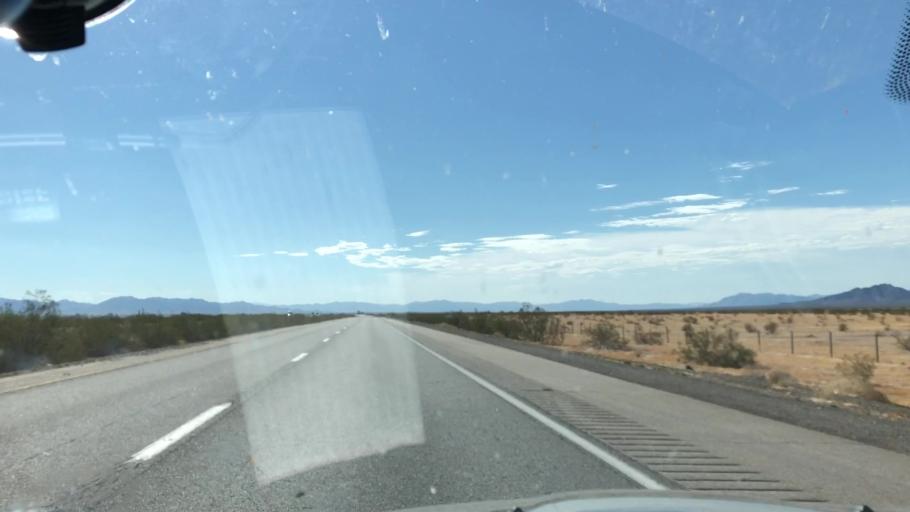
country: US
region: California
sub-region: Riverside County
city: Mesa Verde
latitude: 33.6186
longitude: -115.0271
